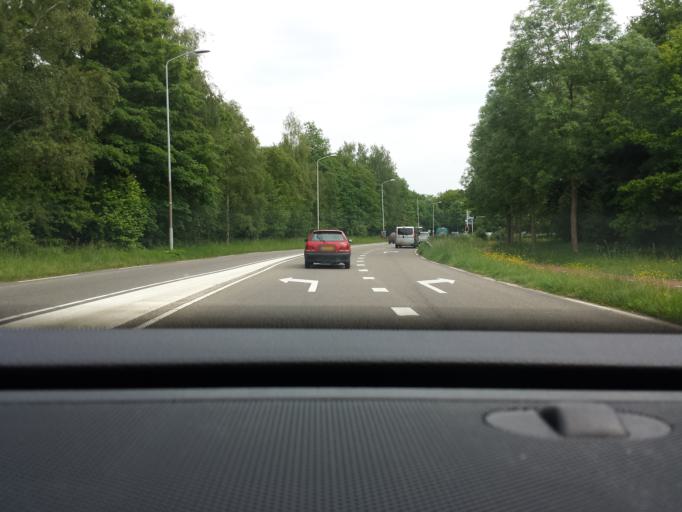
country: NL
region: Gelderland
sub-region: Gemeente Doetinchem
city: Doetinchem
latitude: 51.9614
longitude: 6.2750
